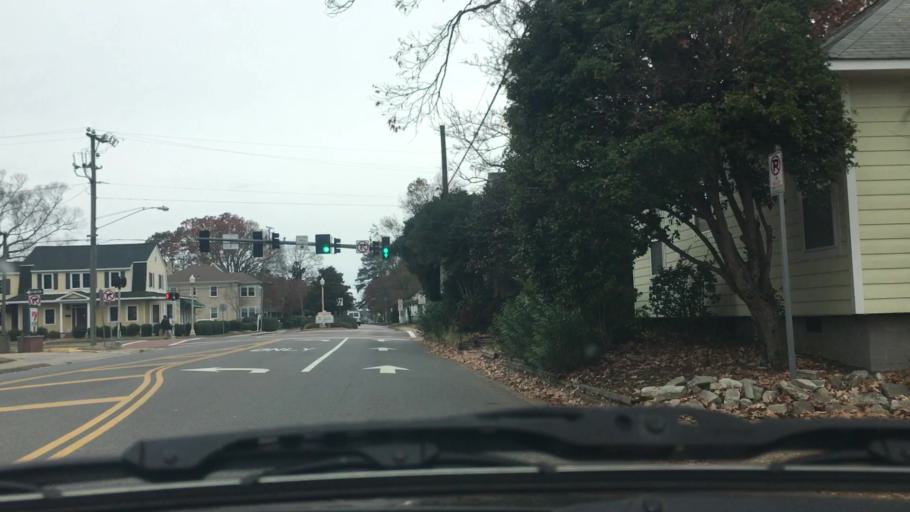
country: US
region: Virginia
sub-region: City of Virginia Beach
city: Virginia Beach
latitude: 36.8489
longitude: -75.9803
